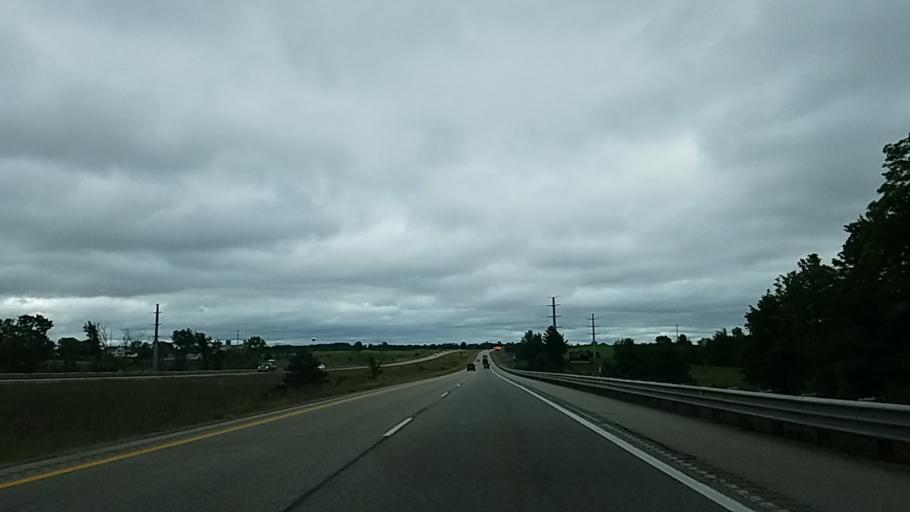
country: US
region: Michigan
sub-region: Otsego County
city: Gaylord
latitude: 45.0607
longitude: -84.6887
